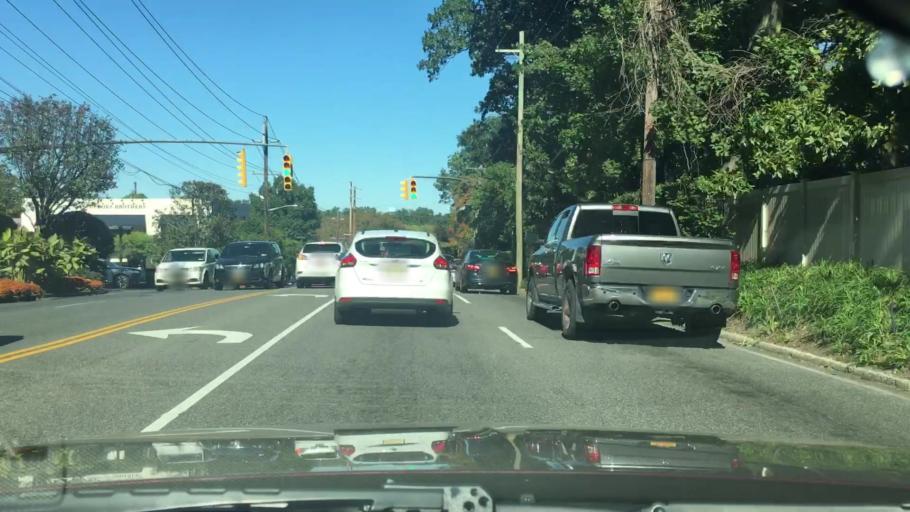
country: US
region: New York
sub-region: Nassau County
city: Roslyn Estates
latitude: 40.7954
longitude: -73.6685
